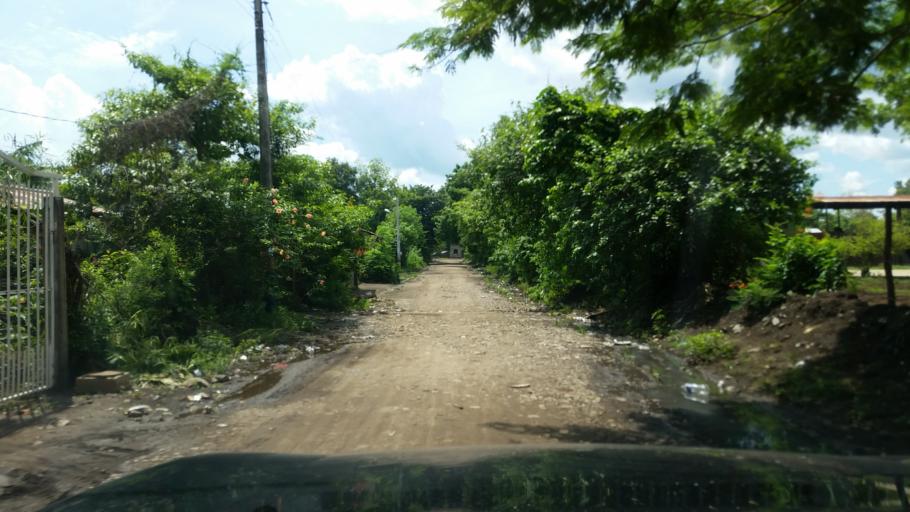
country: NI
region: Chinandega
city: Puerto Morazan
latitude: 12.7696
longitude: -87.1324
